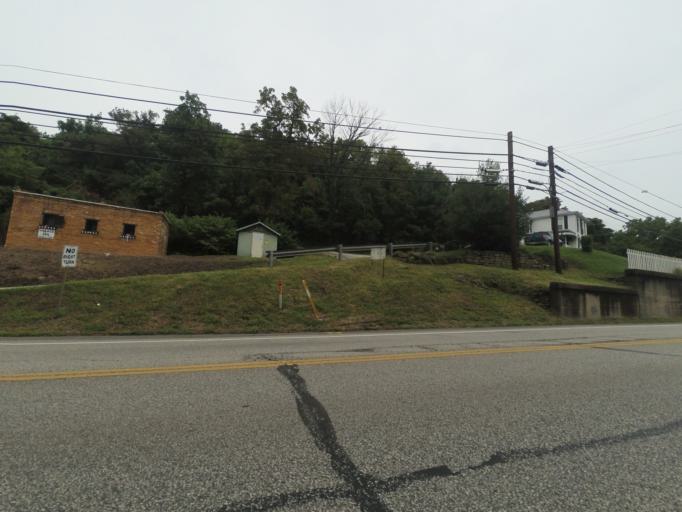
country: US
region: West Virginia
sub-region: Cabell County
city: Huntington
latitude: 38.4282
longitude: -82.4473
